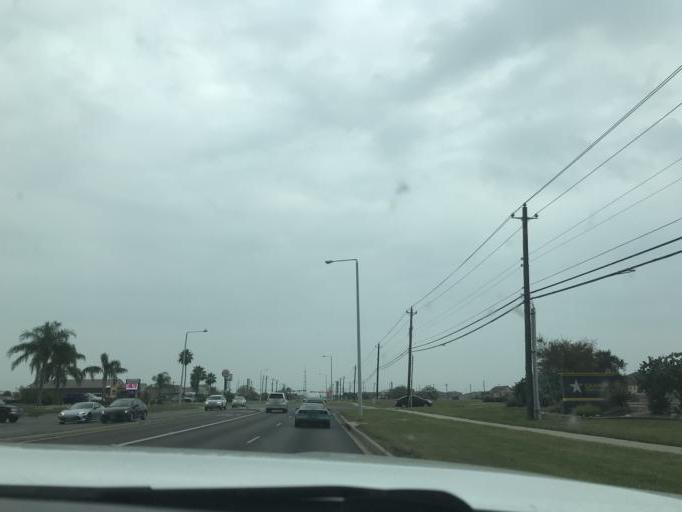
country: US
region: Texas
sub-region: Nueces County
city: Corpus Christi
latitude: 27.6774
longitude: -97.3678
